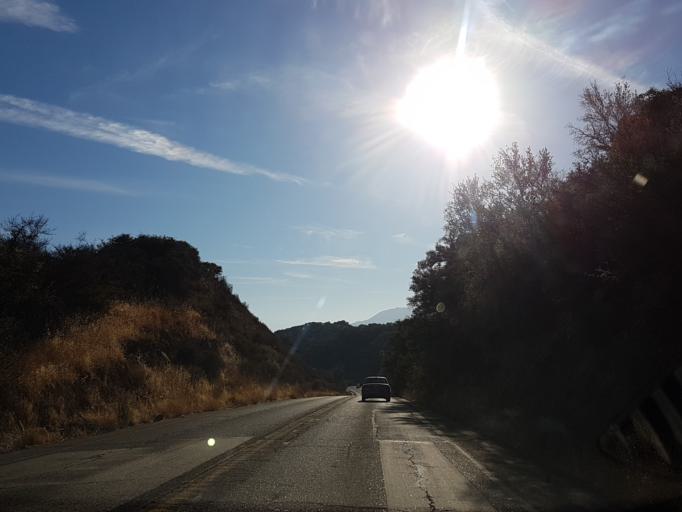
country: US
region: California
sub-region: Santa Barbara County
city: Santa Ynez
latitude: 34.5623
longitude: -119.9289
